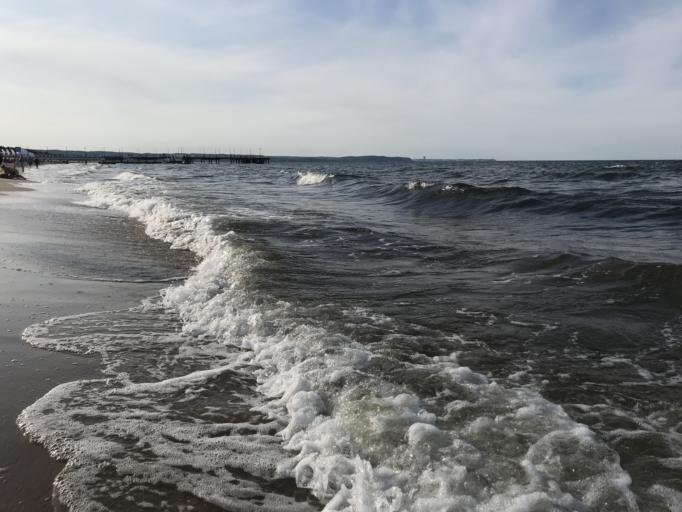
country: PL
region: Pomeranian Voivodeship
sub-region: Gdansk
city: Gdansk
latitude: 54.4125
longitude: 18.6287
